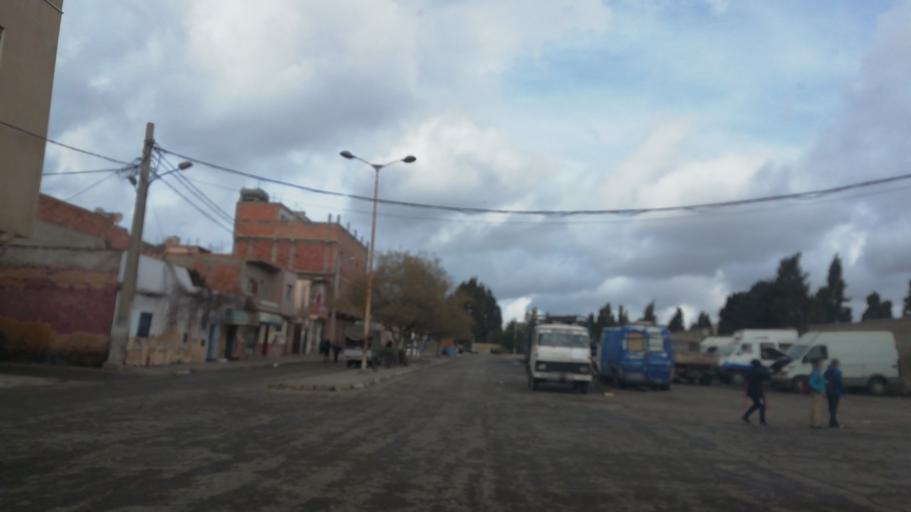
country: DZ
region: Oran
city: Oran
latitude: 35.6876
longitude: -0.6354
